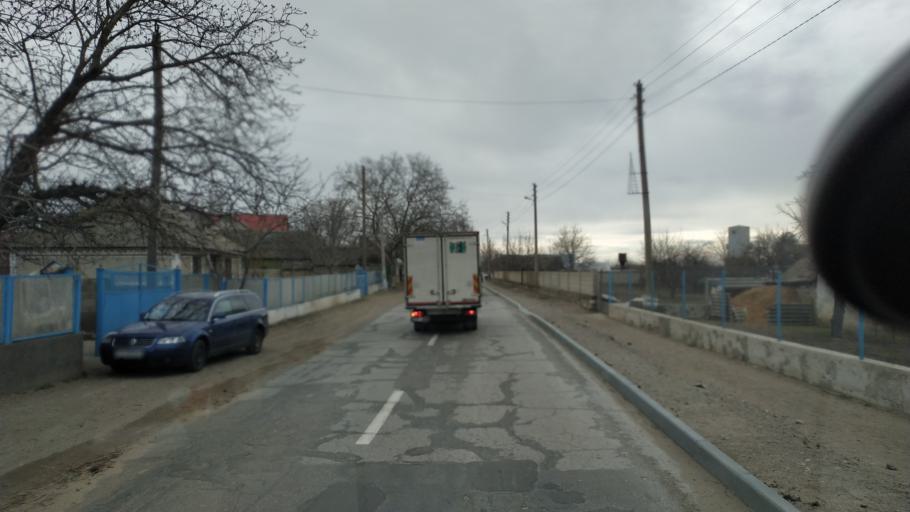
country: MD
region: Telenesti
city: Cocieri
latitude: 47.3146
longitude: 29.1049
